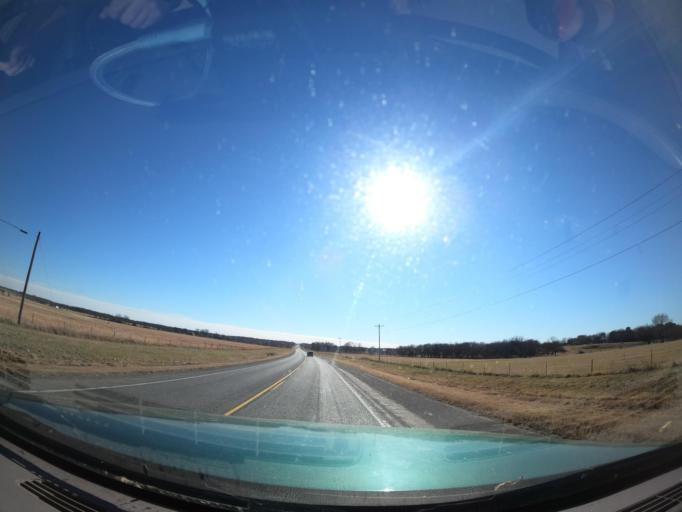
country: US
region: Oklahoma
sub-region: Muskogee County
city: Haskell
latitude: 35.8610
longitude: -95.6774
